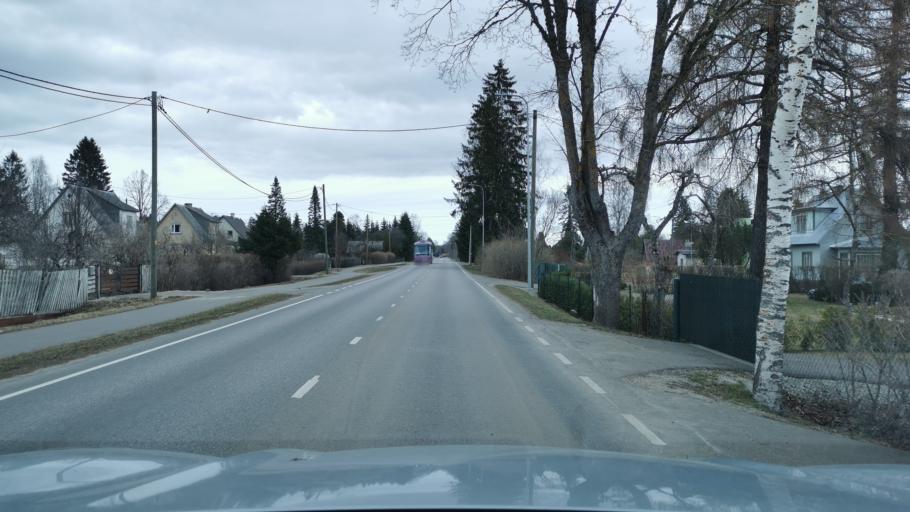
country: EE
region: Ida-Virumaa
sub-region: Kivioli linn
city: Kivioli
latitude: 59.3390
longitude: 27.0112
